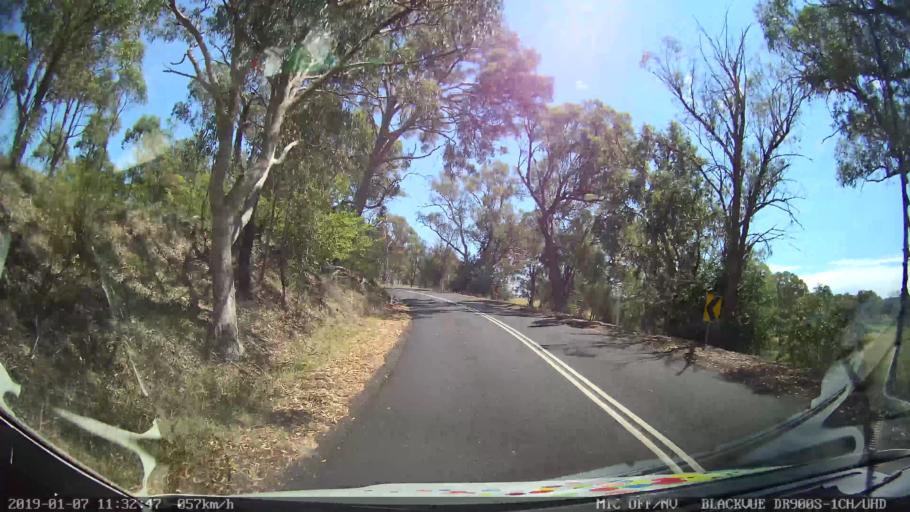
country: AU
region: New South Wales
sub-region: Armidale Dumaresq
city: Armidale
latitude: -30.4060
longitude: 151.5603
